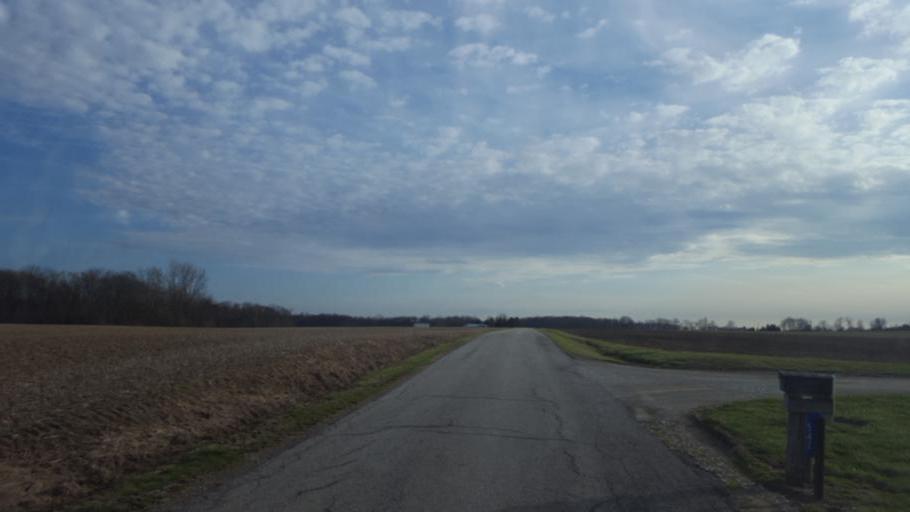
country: US
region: Ohio
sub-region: Crawford County
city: Bucyrus
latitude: 40.7241
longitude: -82.9368
